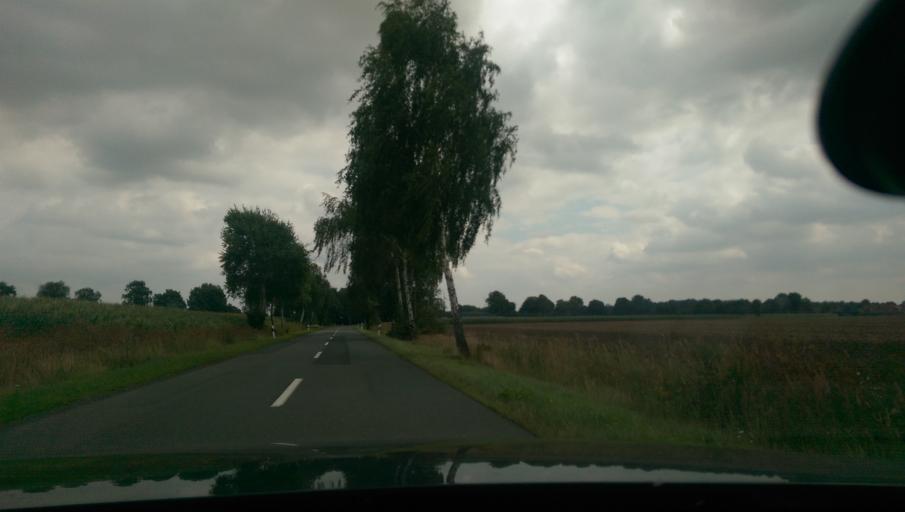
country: DE
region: Lower Saxony
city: Frankenfeld
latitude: 52.7036
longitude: 9.4725
